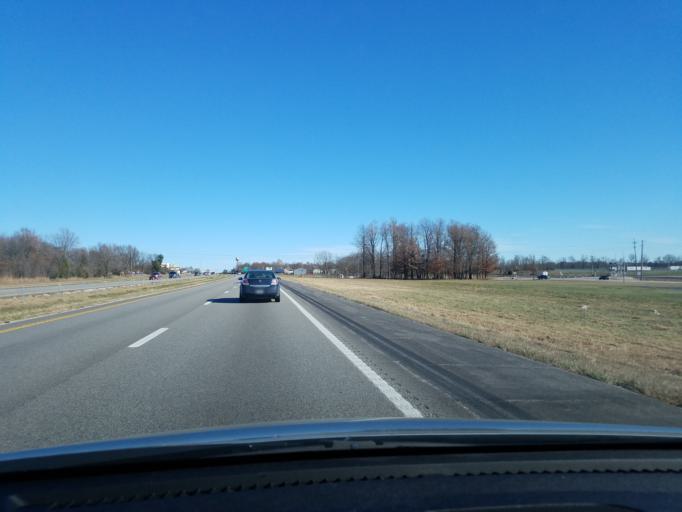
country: US
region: Missouri
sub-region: Greene County
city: Strafford
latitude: 37.2653
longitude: -93.1390
